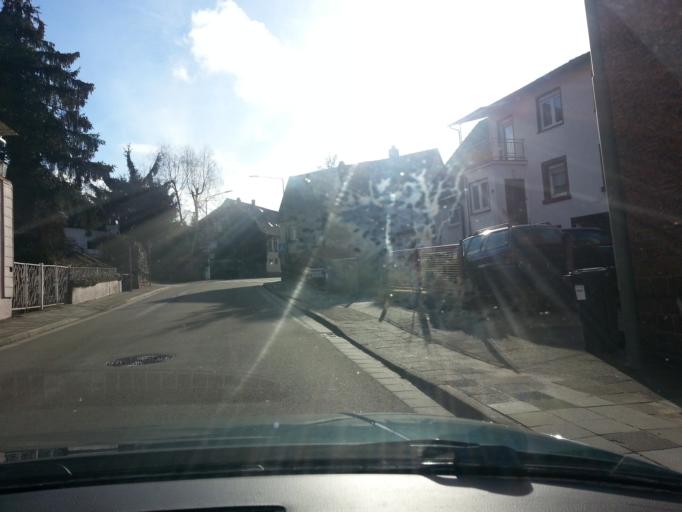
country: DE
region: Rheinland-Pfalz
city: Katzweiler
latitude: 49.4684
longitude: 7.6898
